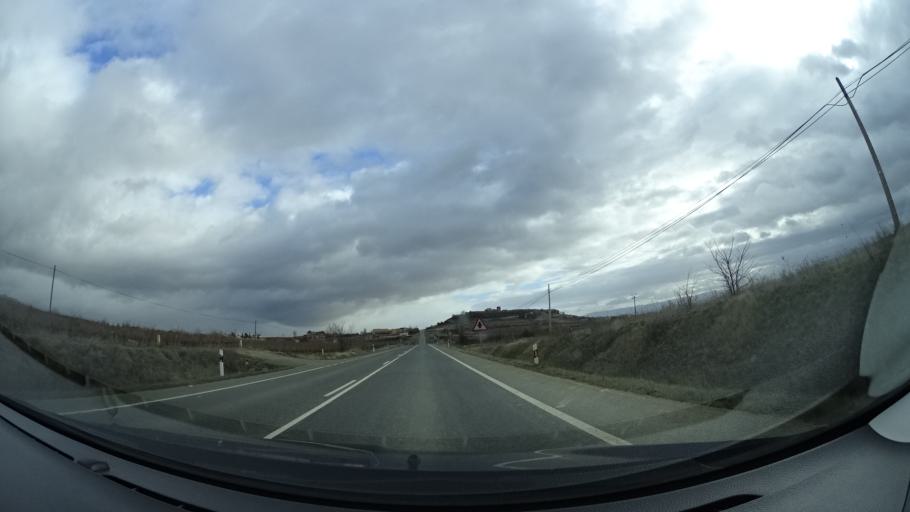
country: ES
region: Basque Country
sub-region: Provincia de Alava
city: Laguardia
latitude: 42.5640
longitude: -2.5998
